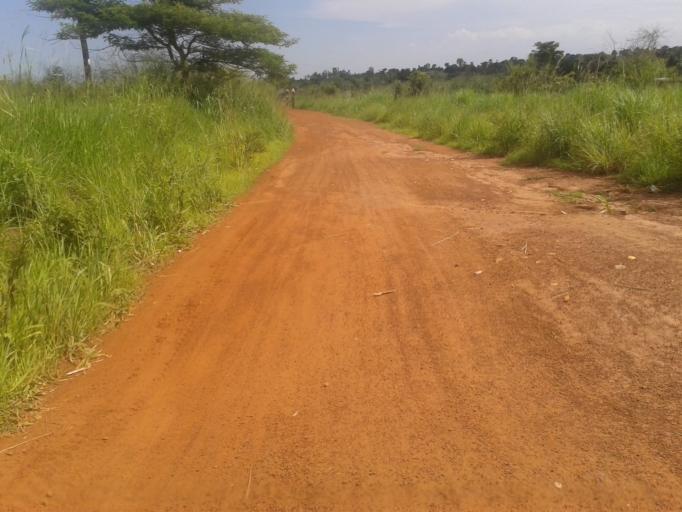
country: UG
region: Northern Region
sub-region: Gulu District
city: Gulu
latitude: 2.8202
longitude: 32.2685
